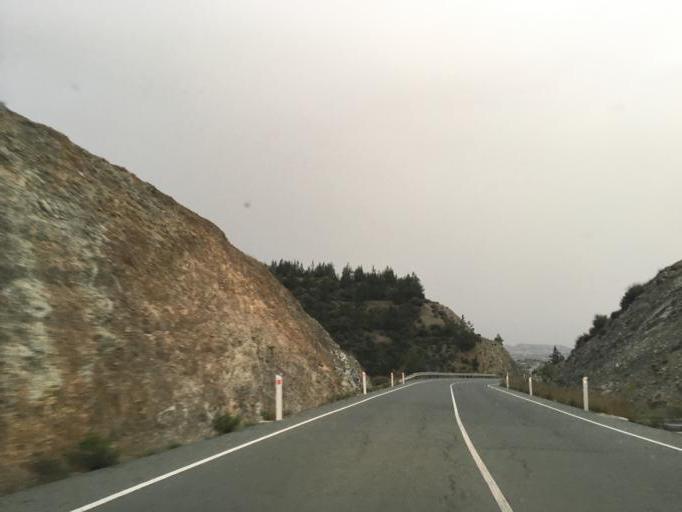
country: CY
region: Limassol
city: Parekklisha
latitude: 34.7946
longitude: 33.1577
